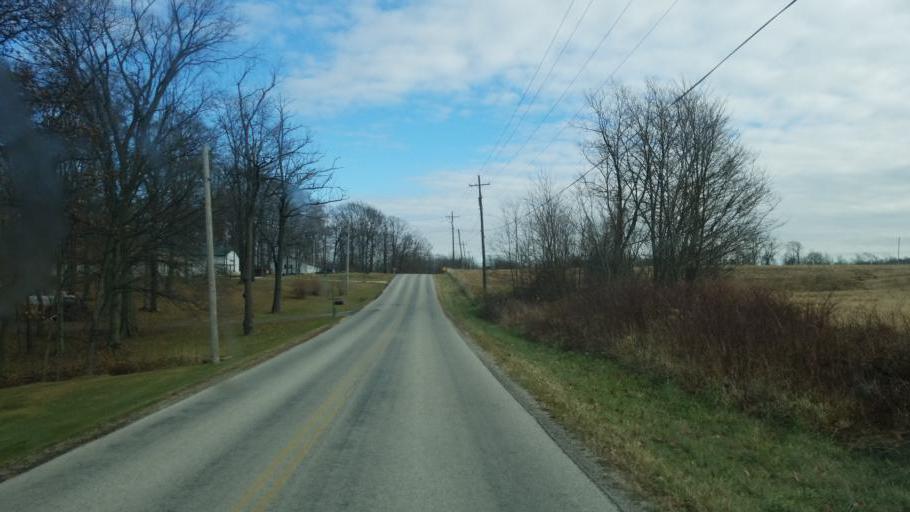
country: US
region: Ohio
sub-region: Richland County
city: Ontario
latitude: 40.7908
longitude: -82.6091
